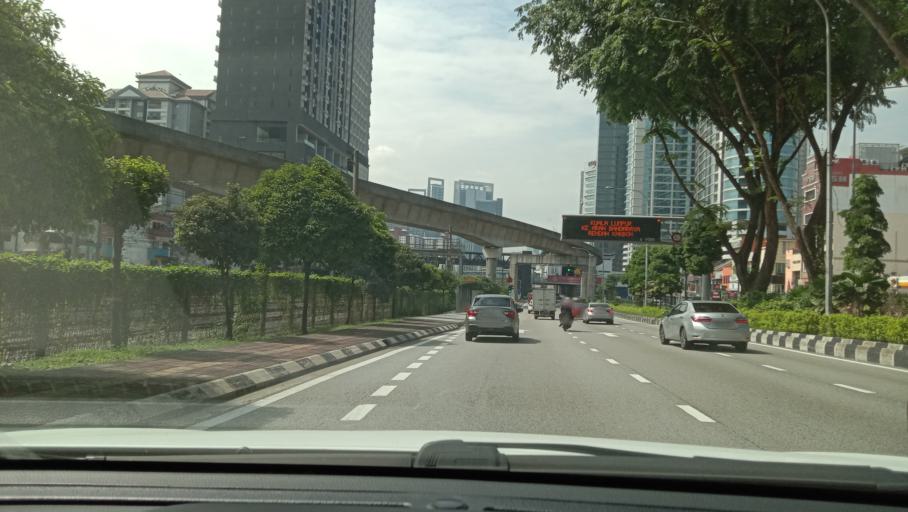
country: MY
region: Kuala Lumpur
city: Kuala Lumpur
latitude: 3.1298
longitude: 101.6809
